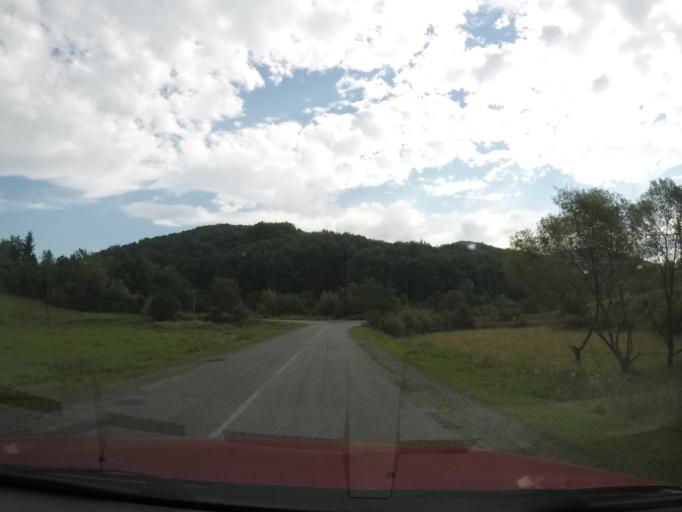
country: UA
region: Zakarpattia
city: Velykyi Bereznyi
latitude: 48.9528
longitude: 22.5462
